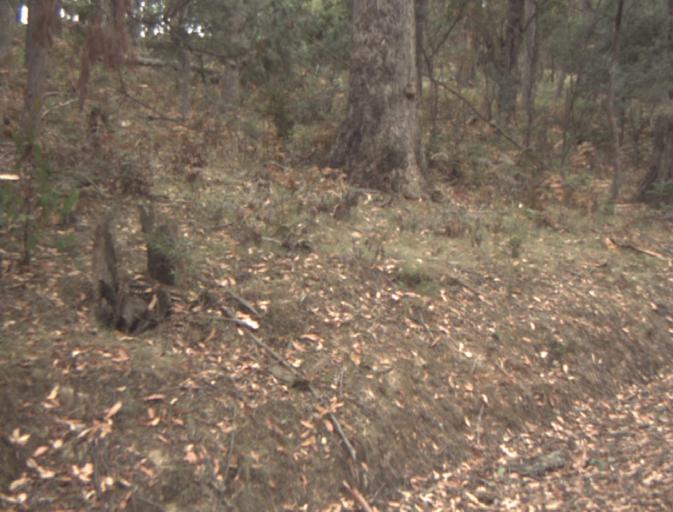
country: AU
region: Tasmania
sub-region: Northern Midlands
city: Evandale
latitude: -41.4933
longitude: 147.5482
